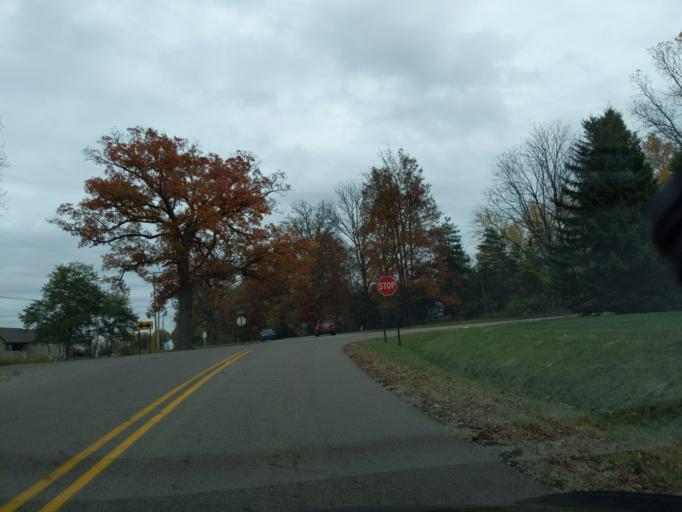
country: US
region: Michigan
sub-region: Eaton County
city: Eaton Rapids
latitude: 42.5241
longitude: -84.6020
